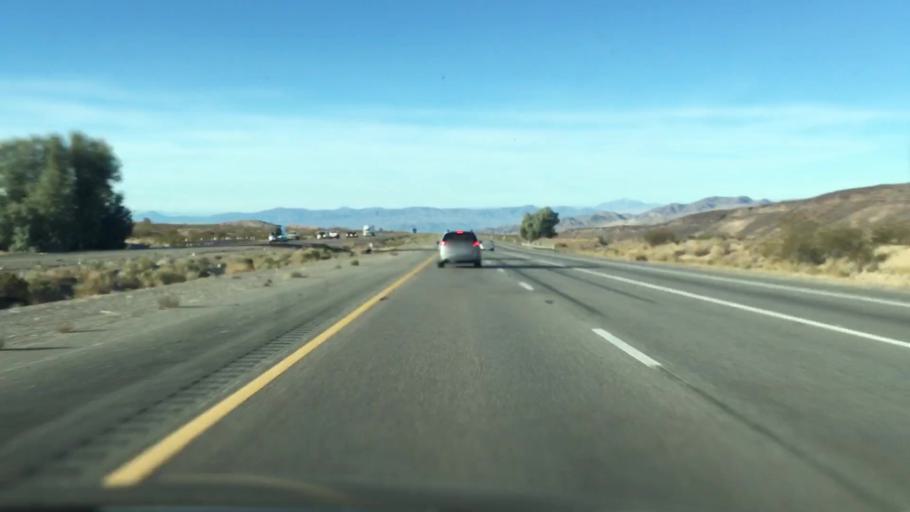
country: US
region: Nevada
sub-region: Clark County
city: Sandy Valley
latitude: 35.3901
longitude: -115.8409
